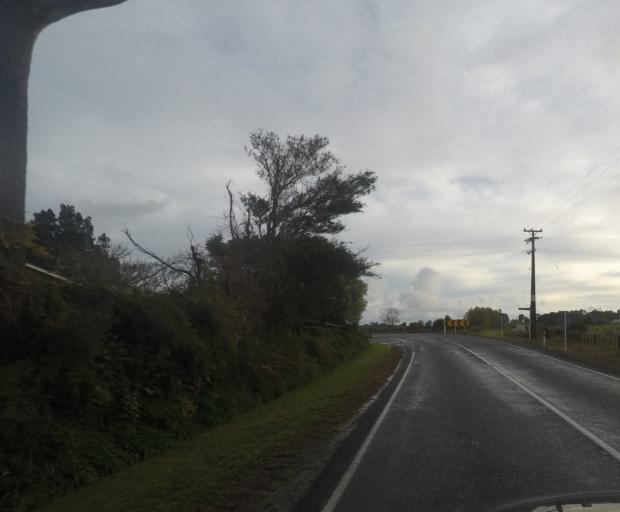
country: NZ
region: Auckland
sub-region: Auckland
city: Wellsford
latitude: -36.1986
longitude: 174.5813
